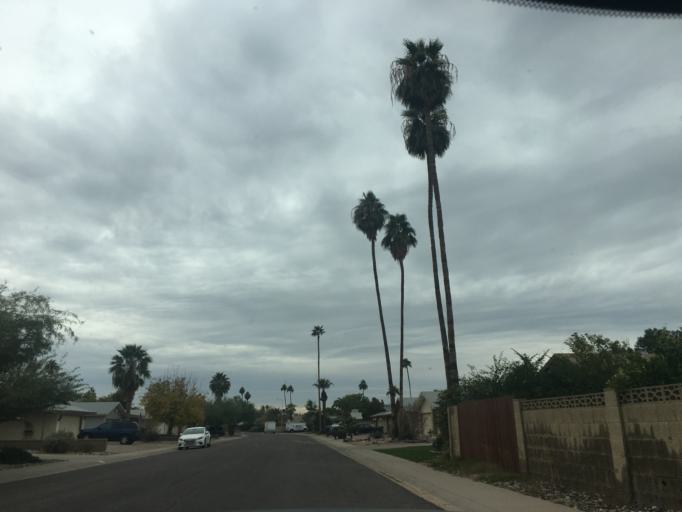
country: US
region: Arizona
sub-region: Maricopa County
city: Tempe
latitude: 33.3827
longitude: -111.9186
